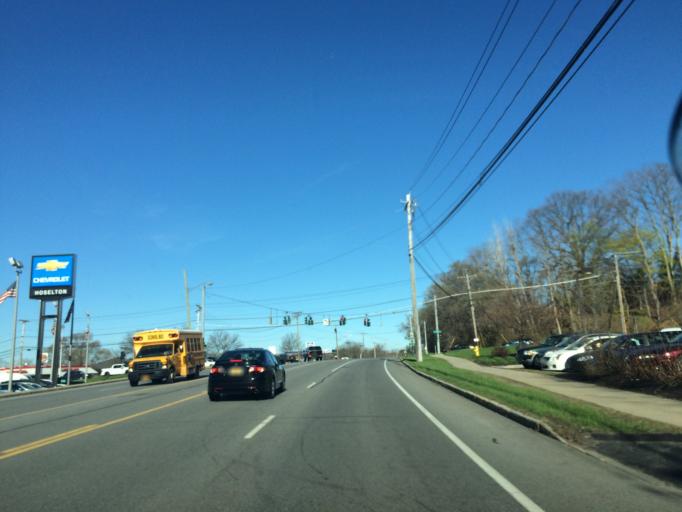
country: US
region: New York
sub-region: Monroe County
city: East Rochester
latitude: 43.1025
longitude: -77.4798
